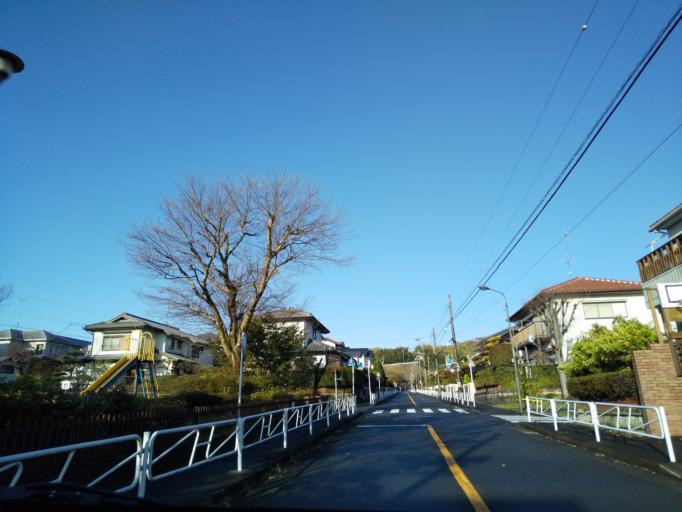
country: JP
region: Tokyo
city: Hachioji
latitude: 35.6255
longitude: 139.3547
